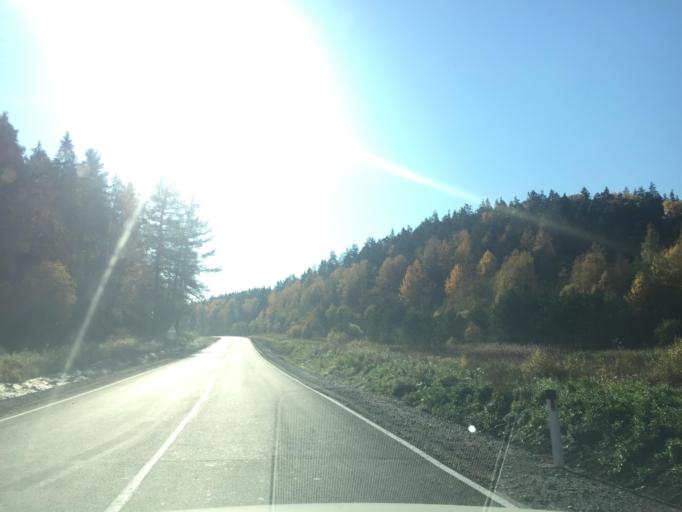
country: RU
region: Leningrad
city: Kuznechnoye
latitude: 61.3291
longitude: 29.8632
